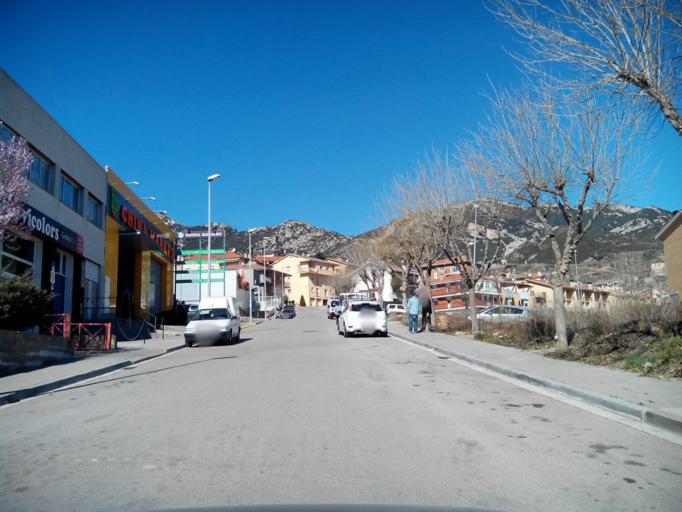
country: ES
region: Catalonia
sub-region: Provincia de Barcelona
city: Berga
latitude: 42.0949
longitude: 1.8504
